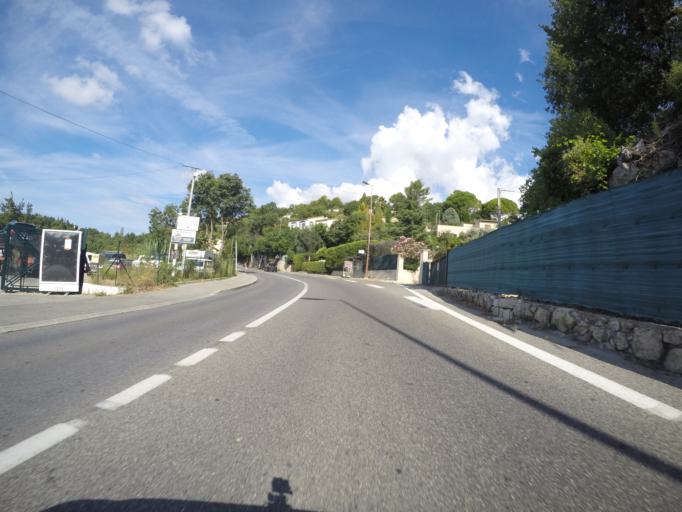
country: FR
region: Provence-Alpes-Cote d'Azur
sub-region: Departement des Alpes-Maritimes
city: Opio
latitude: 43.6776
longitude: 6.9799
